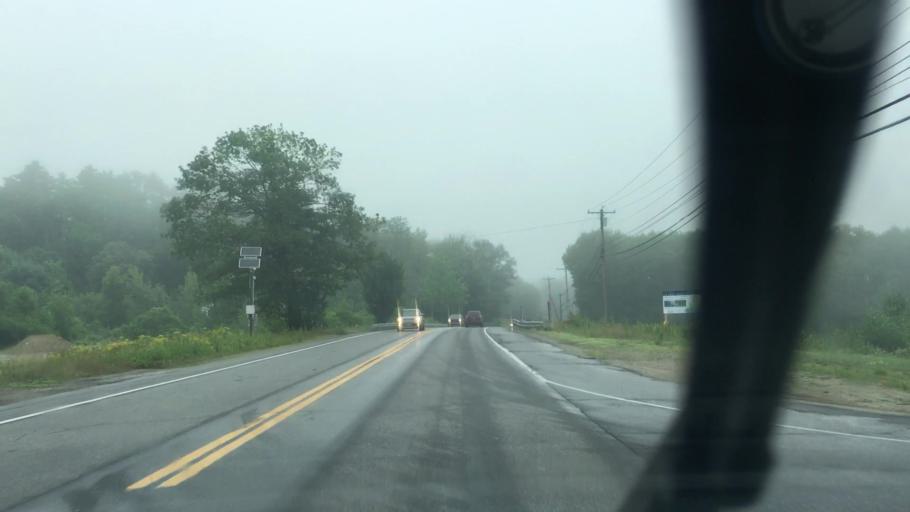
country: US
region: Maine
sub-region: Lincoln County
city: Wiscasset
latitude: 43.9954
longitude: -69.6850
